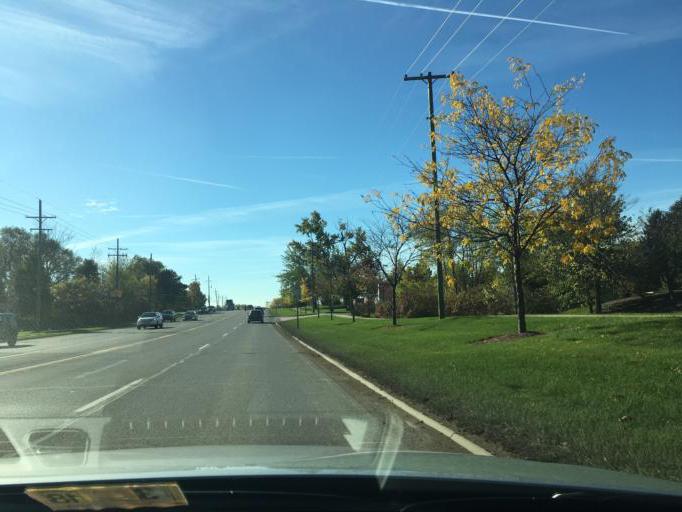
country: US
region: Michigan
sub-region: Wayne County
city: Plymouth
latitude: 42.3933
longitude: -83.5103
